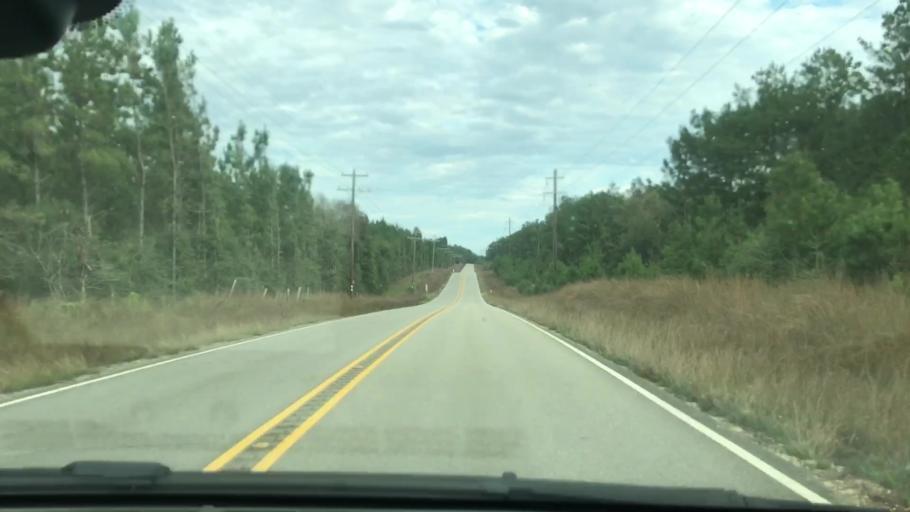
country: US
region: Louisiana
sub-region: Saint Tammany Parish
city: Abita Springs
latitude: 30.5294
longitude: -89.9144
